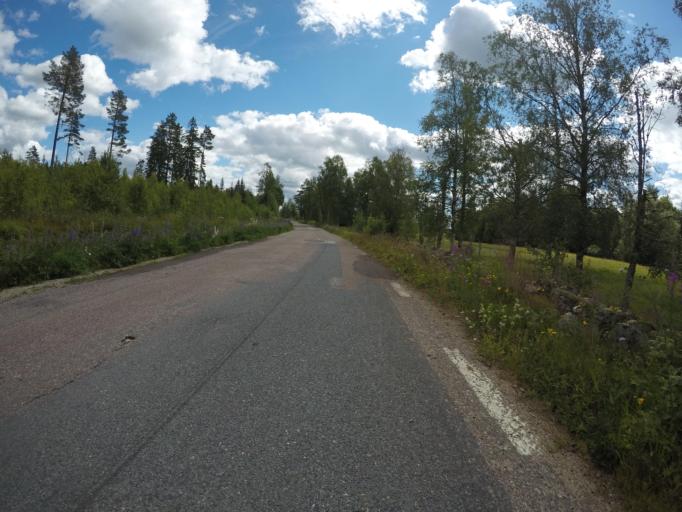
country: SE
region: OErebro
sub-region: Hallefors Kommun
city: Haellefors
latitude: 60.0512
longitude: 14.5014
